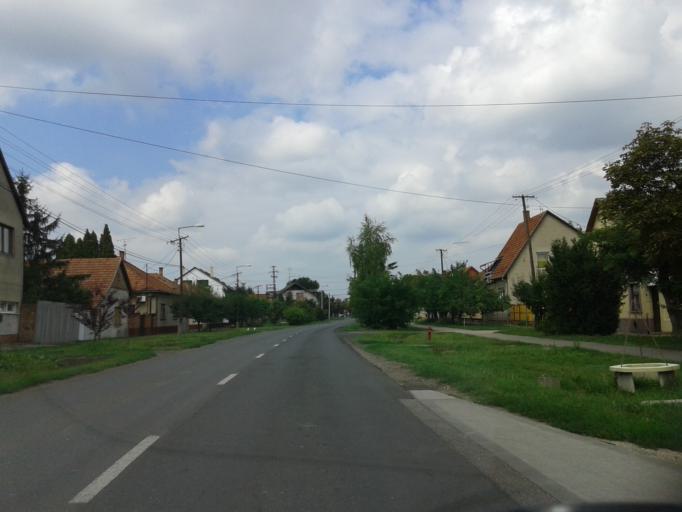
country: HU
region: Csongrad
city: Domaszek
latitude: 46.2761
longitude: 20.0582
